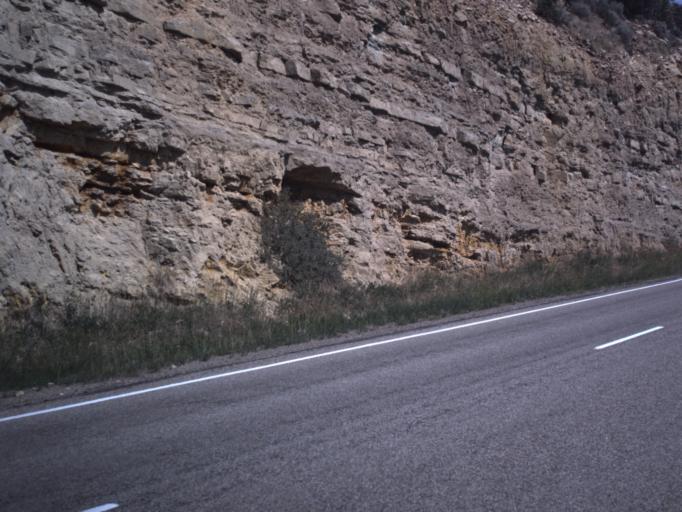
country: US
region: Utah
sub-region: Daggett County
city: Manila
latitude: 40.9054
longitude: -109.7000
